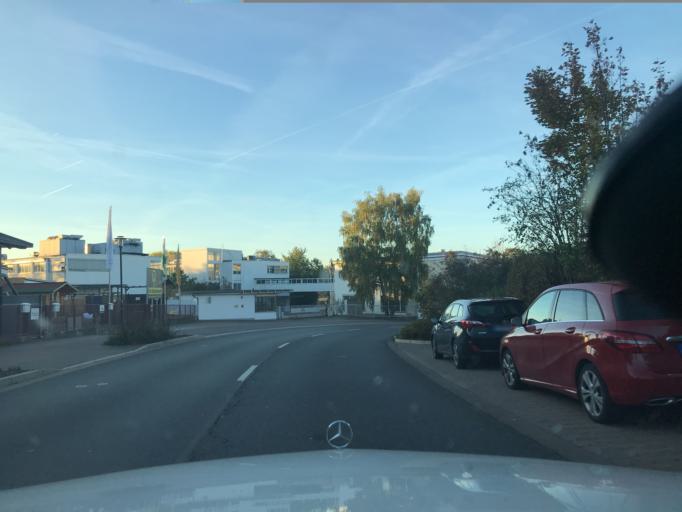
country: DE
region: Hesse
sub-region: Regierungsbezirk Kassel
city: Eschwege
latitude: 51.1895
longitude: 10.0437
